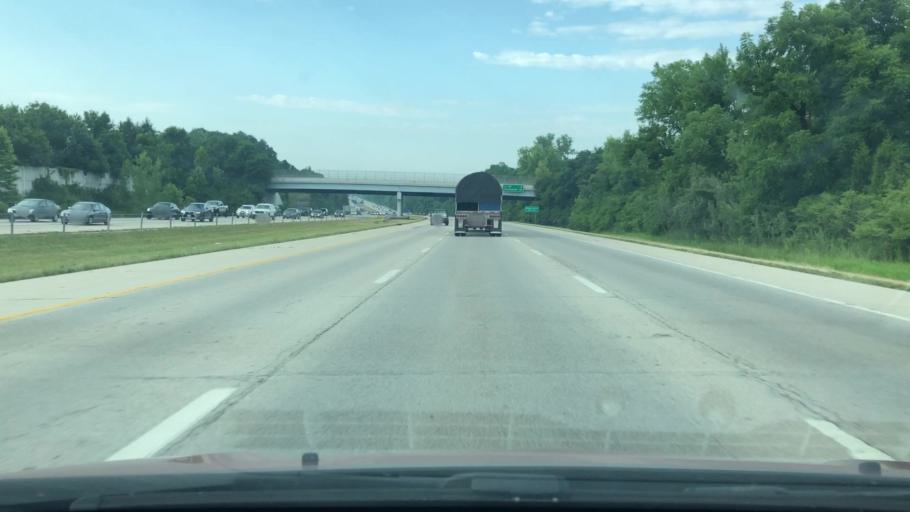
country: US
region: Ohio
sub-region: Greene County
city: Beavercreek
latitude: 39.6845
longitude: -84.1002
